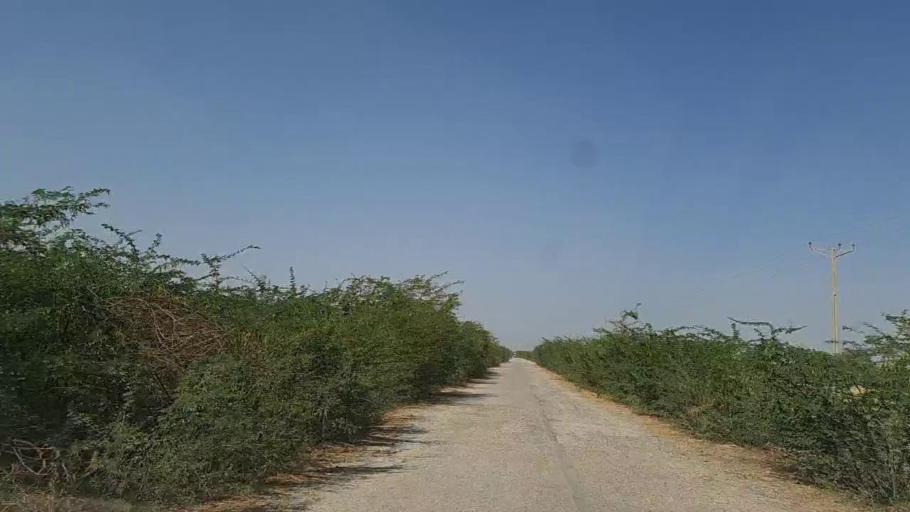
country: PK
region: Sindh
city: Naukot
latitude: 24.6343
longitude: 69.2882
